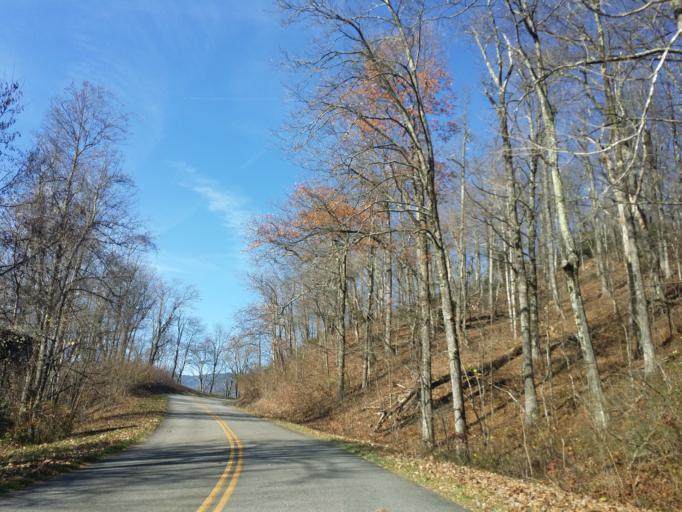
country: US
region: North Carolina
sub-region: Mitchell County
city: Spruce Pine
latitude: 35.7807
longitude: -82.1603
